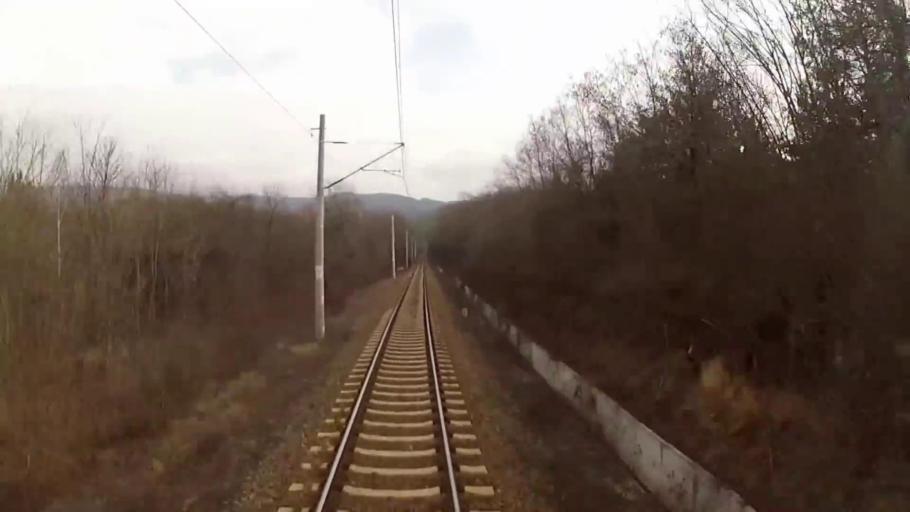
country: BG
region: Sofiya
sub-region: Obshtina Mirkovo
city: Mirkovo
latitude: 42.7190
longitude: 23.8768
